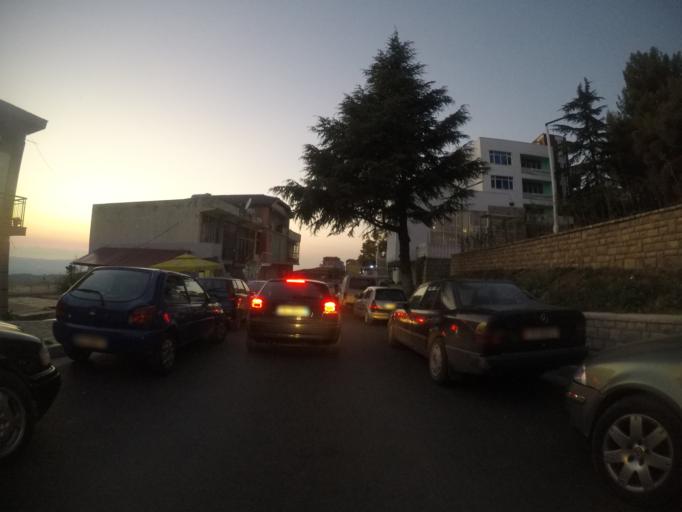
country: AL
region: Durres
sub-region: Rrethi i Krujes
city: Kruje
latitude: 41.5101
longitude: 19.7932
